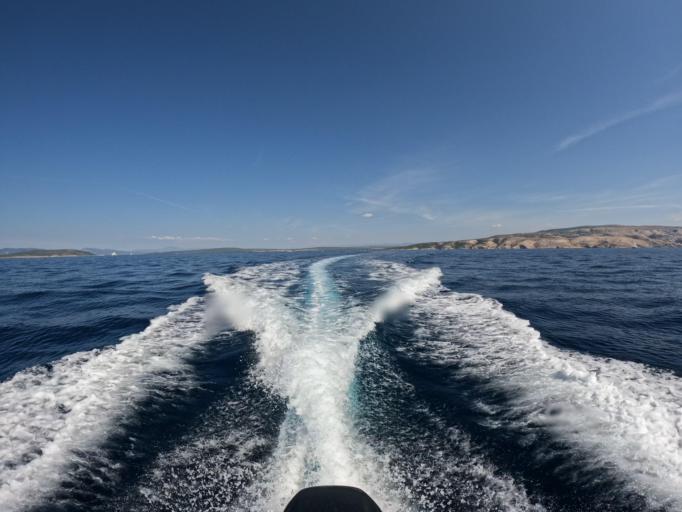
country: HR
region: Primorsko-Goranska
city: Punat
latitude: 44.9370
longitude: 14.6160
